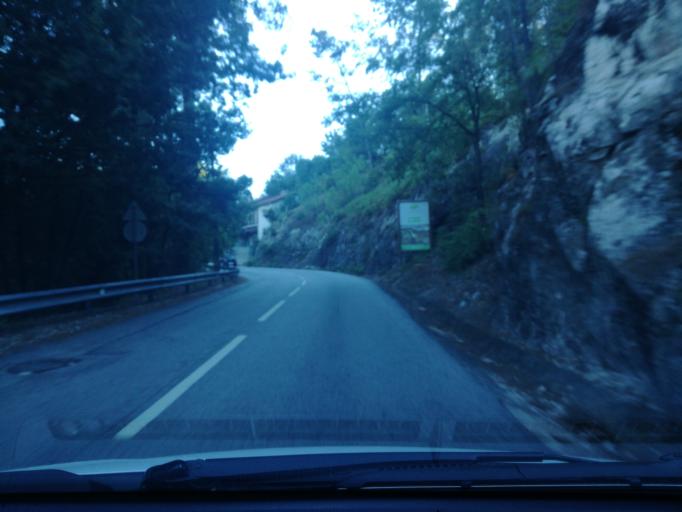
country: PT
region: Braga
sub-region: Vieira do Minho
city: Real
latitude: 41.6997
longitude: -8.1674
